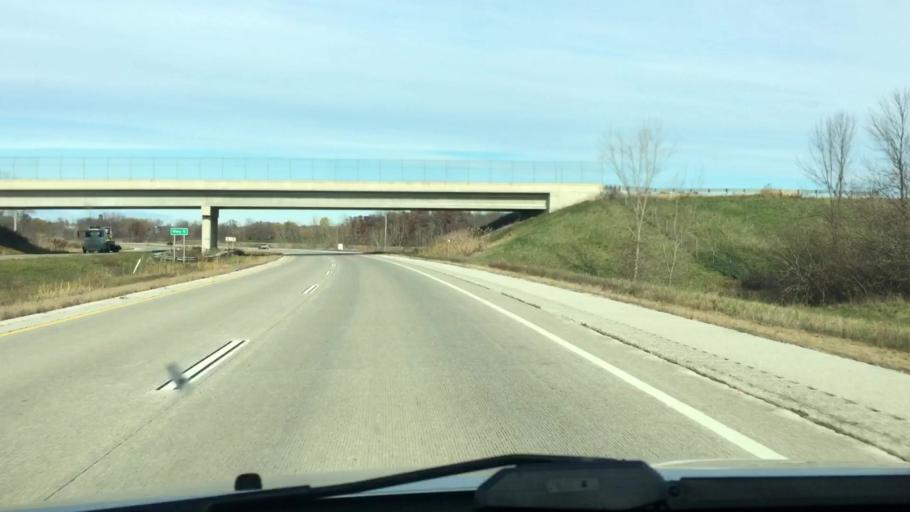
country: US
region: Wisconsin
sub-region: Kewaunee County
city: Luxemburg
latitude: 44.6378
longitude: -87.7551
